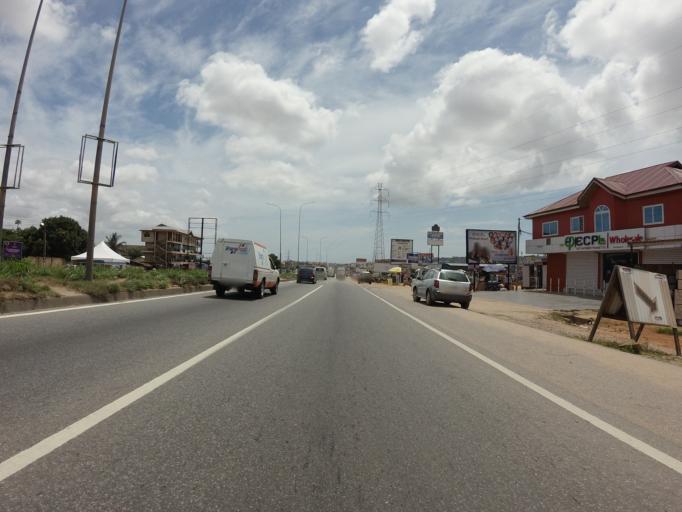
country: GH
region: Greater Accra
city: Gbawe
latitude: 5.5509
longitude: -0.3559
